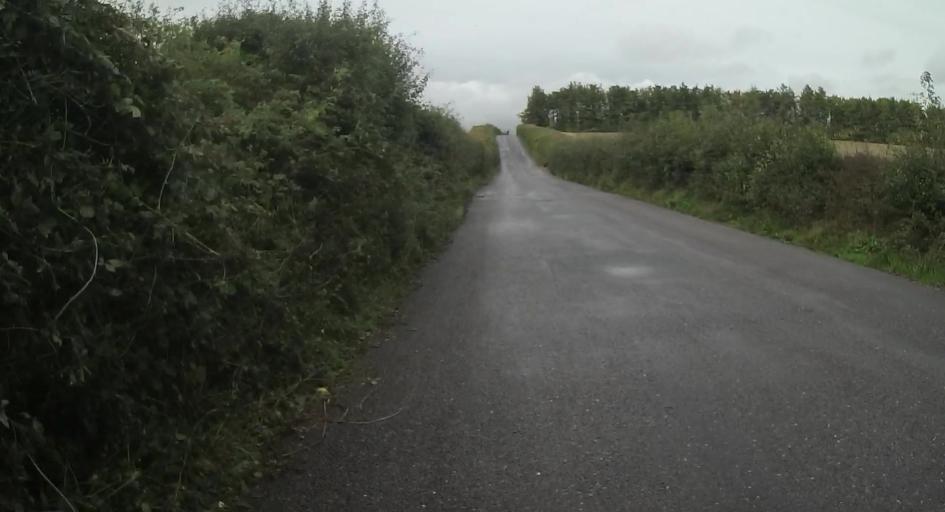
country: GB
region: England
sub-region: Hampshire
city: Tadley
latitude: 51.2927
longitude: -1.1487
